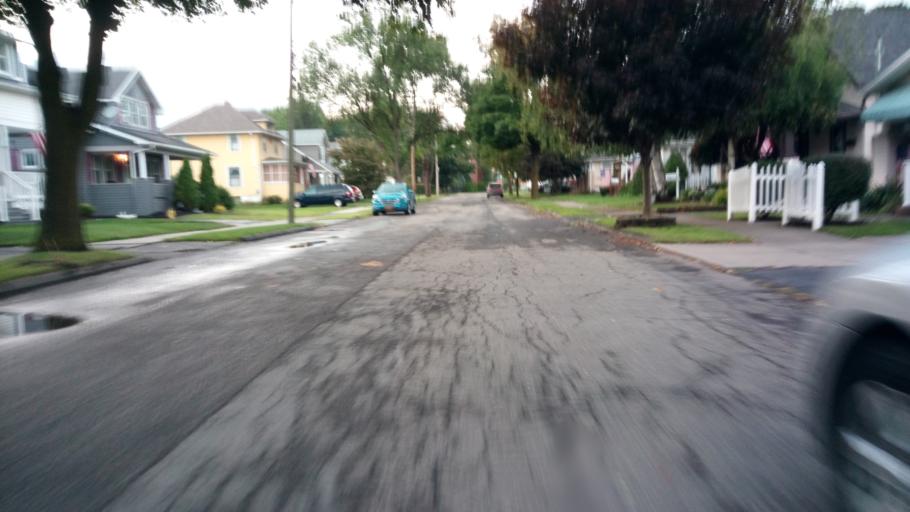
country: US
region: New York
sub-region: Chemung County
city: Elmira
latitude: 42.0977
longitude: -76.8270
